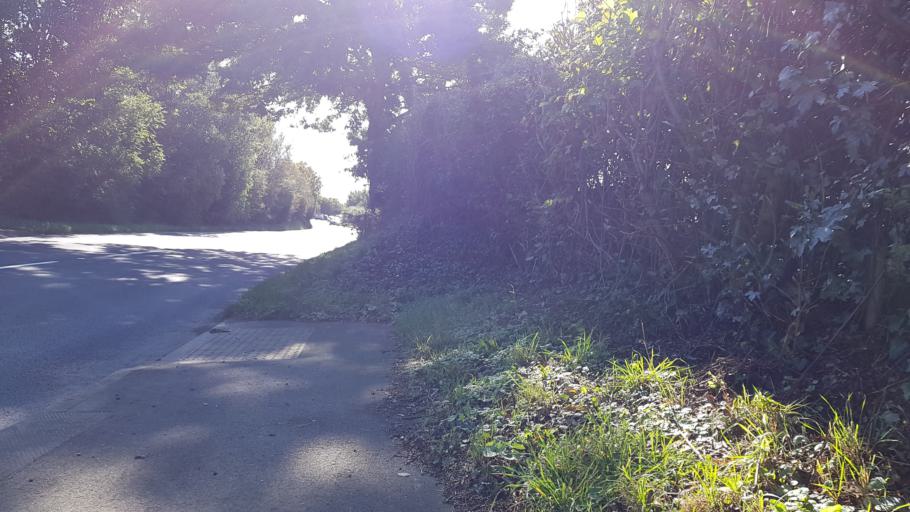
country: GB
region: England
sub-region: Isle of Wight
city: Newport
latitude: 50.6819
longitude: -1.2876
